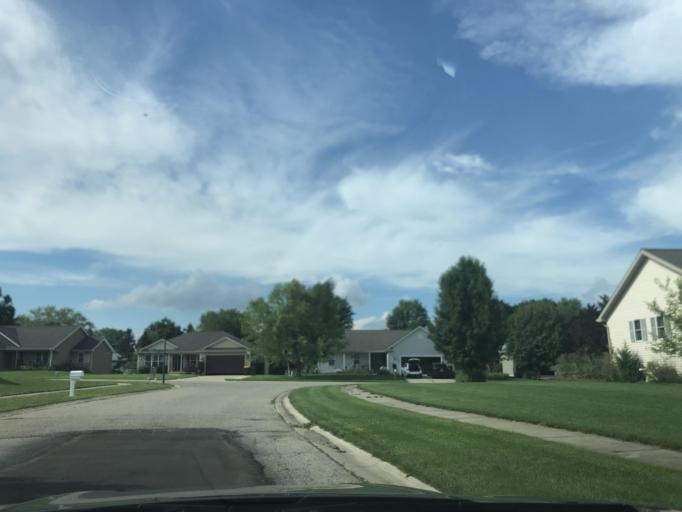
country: US
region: Michigan
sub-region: Ingham County
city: Holt
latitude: 42.6501
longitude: -84.4944
